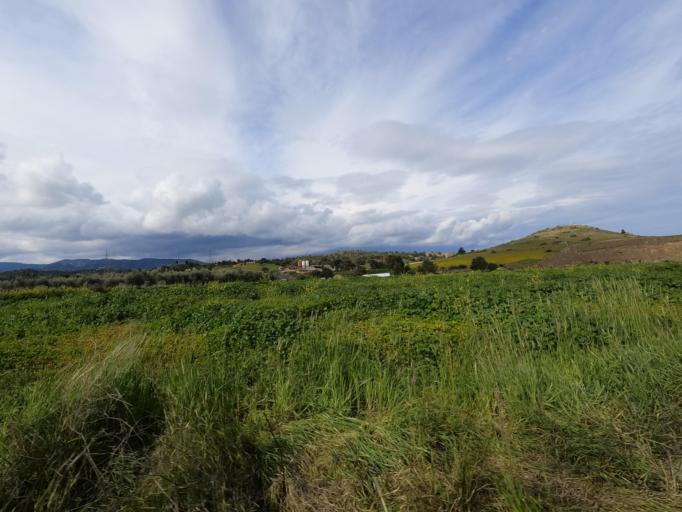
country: CY
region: Lefkosia
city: Lefka
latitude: 35.0740
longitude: 32.9259
